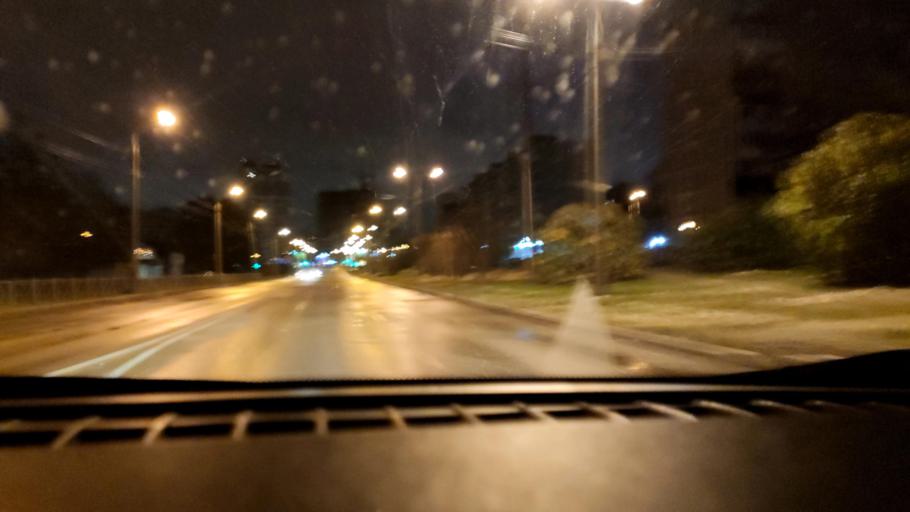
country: RU
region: Perm
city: Perm
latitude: 57.9788
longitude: 56.2086
